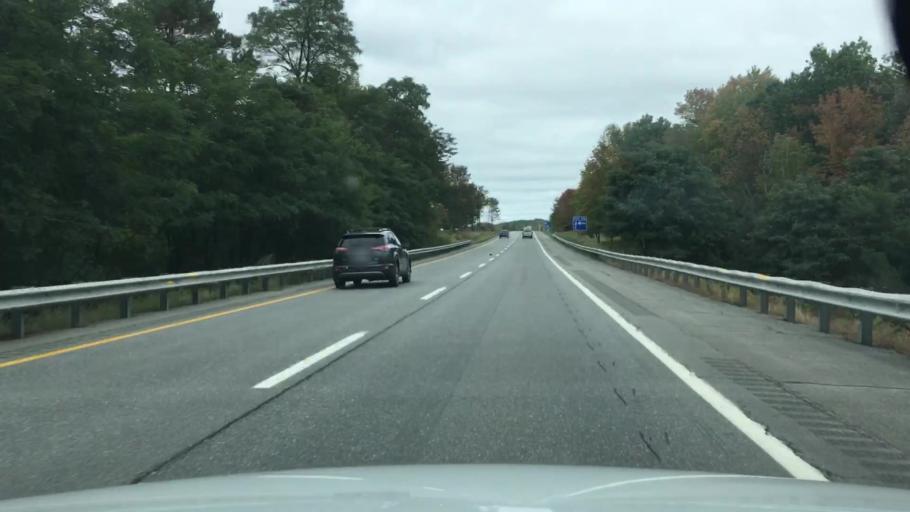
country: US
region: Maine
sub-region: Somerset County
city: Fairfield
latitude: 44.5842
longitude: -69.6237
